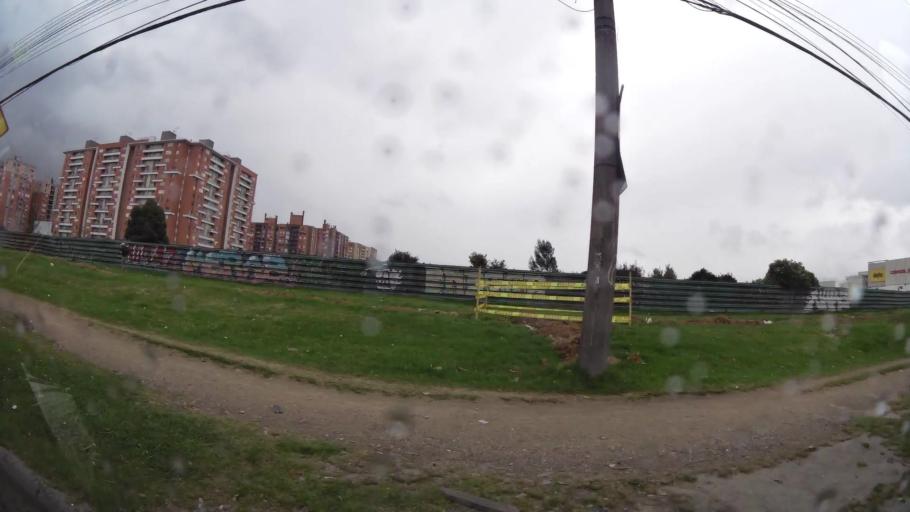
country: CO
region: Bogota D.C.
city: Bogota
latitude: 4.6530
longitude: -74.1297
